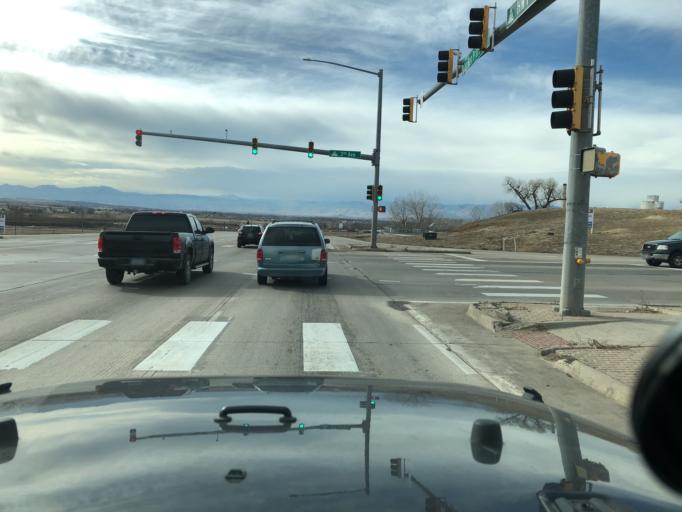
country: US
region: Colorado
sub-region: Boulder County
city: Longmont
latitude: 40.1594
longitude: -105.0657
